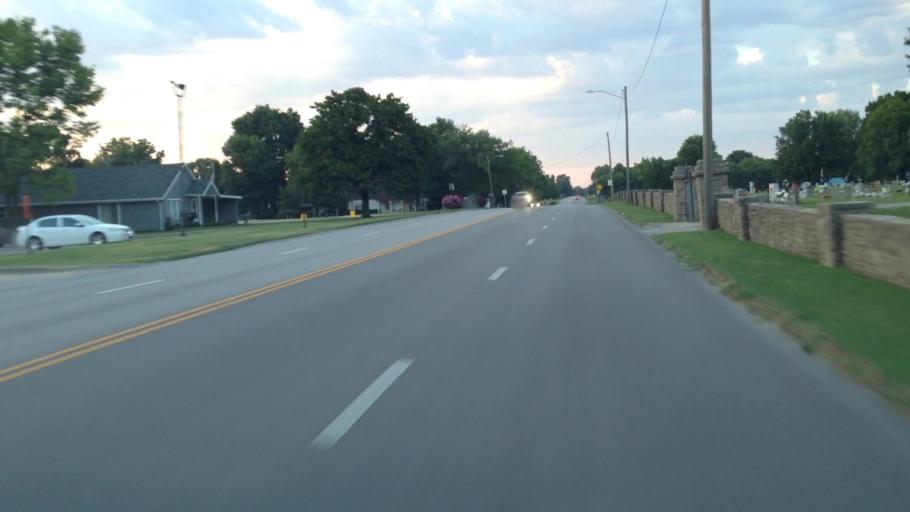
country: US
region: Kansas
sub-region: Montgomery County
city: Independence
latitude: 37.2456
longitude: -95.7062
